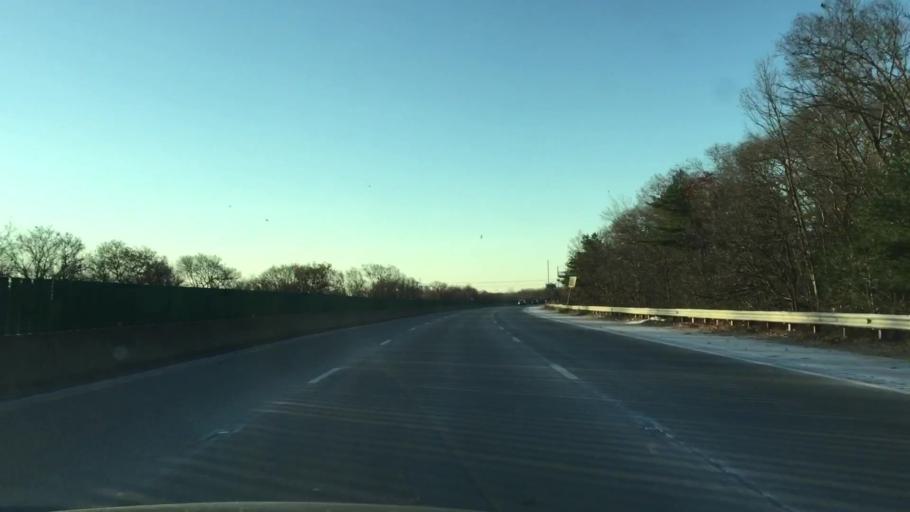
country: US
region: Massachusetts
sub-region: Norfolk County
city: Avon
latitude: 42.1037
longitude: -71.0578
